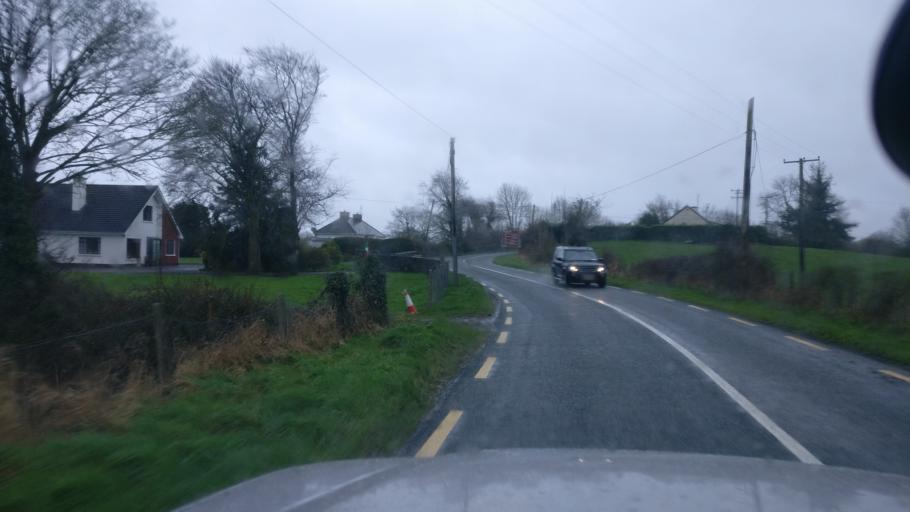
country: IE
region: Connaught
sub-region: County Galway
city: Portumna
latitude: 53.1040
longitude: -8.2230
